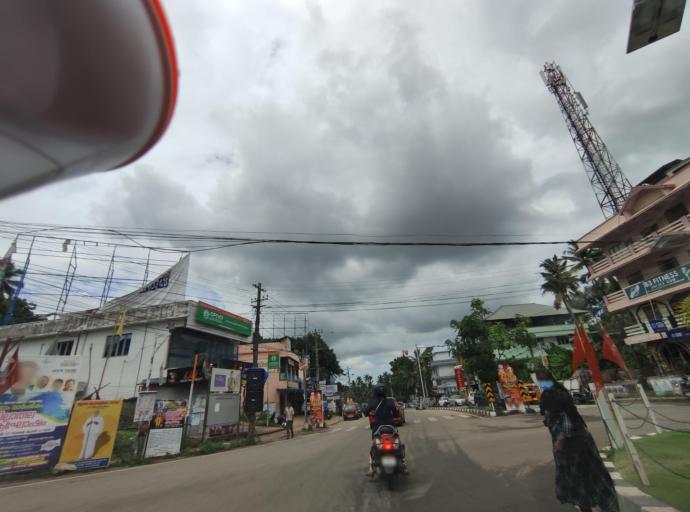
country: IN
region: Kerala
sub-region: Thiruvananthapuram
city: Nedumangad
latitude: 8.5608
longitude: 76.9434
